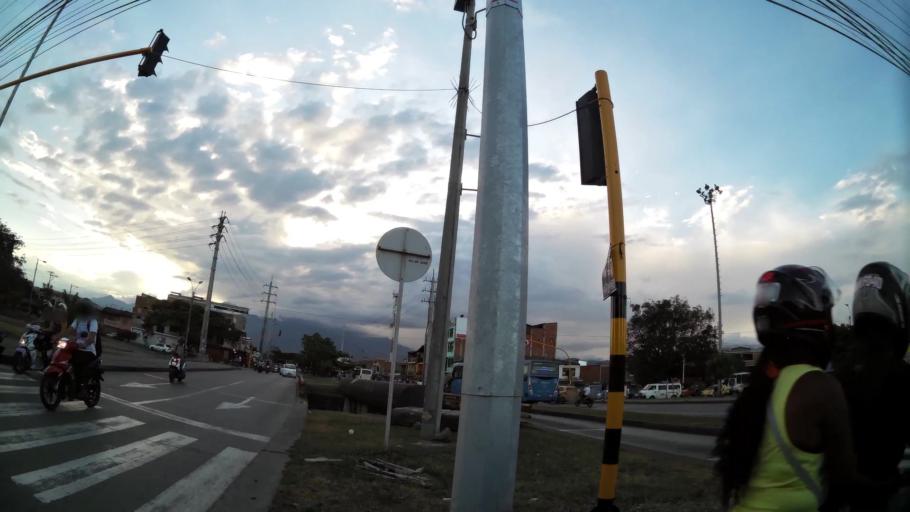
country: CO
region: Valle del Cauca
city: Cali
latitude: 3.4464
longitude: -76.4837
